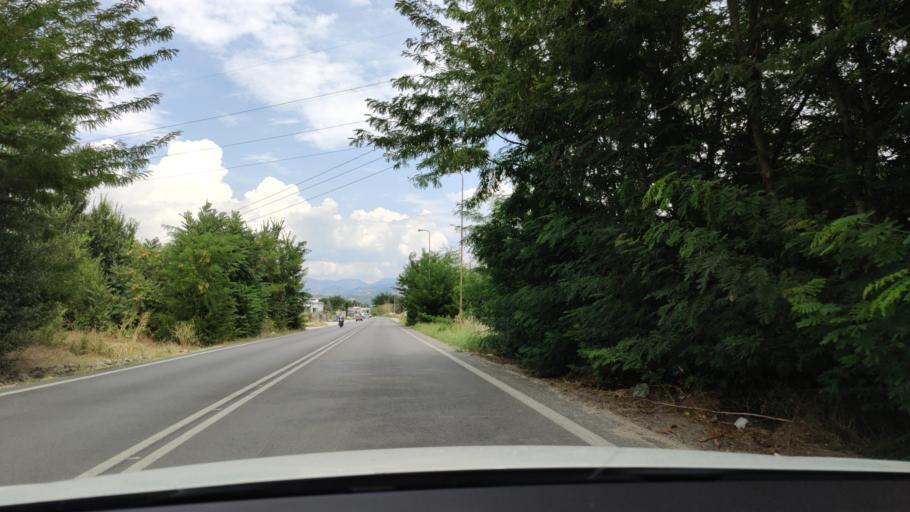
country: GR
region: Central Macedonia
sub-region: Nomos Serron
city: Serres
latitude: 41.0589
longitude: 23.5377
